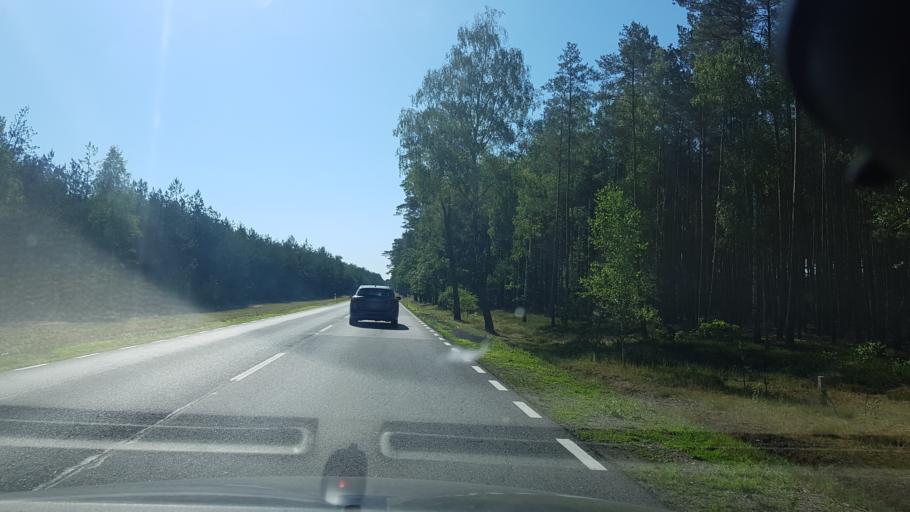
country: PL
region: Masovian Voivodeship
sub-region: Powiat wyszkowski
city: Branszczyk
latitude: 52.5621
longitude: 21.5689
